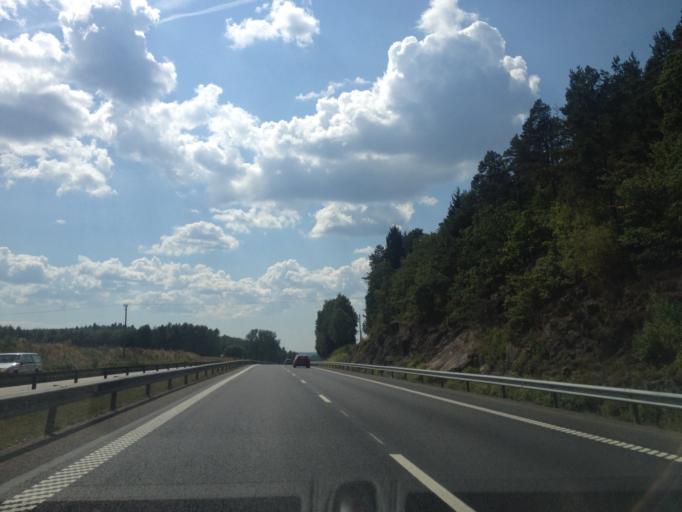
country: SE
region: Vaestra Goetaland
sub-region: Lerums Kommun
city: Stenkullen
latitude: 57.7904
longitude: 12.3352
